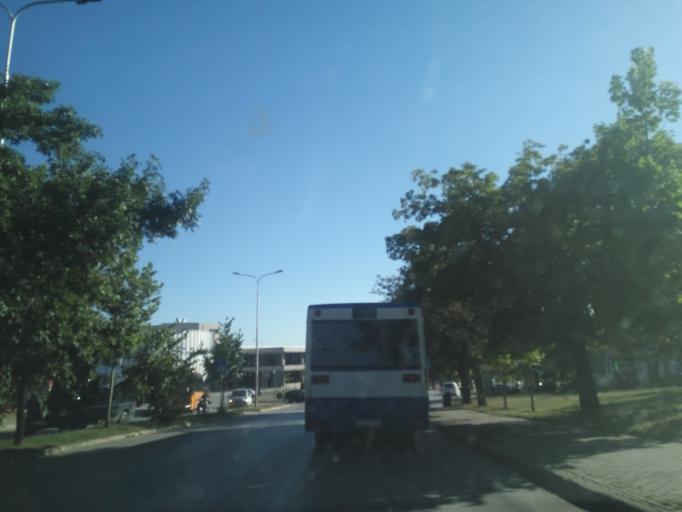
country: XK
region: Pristina
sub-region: Komuna e Prishtines
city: Pristina
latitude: 42.6485
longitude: 21.1633
